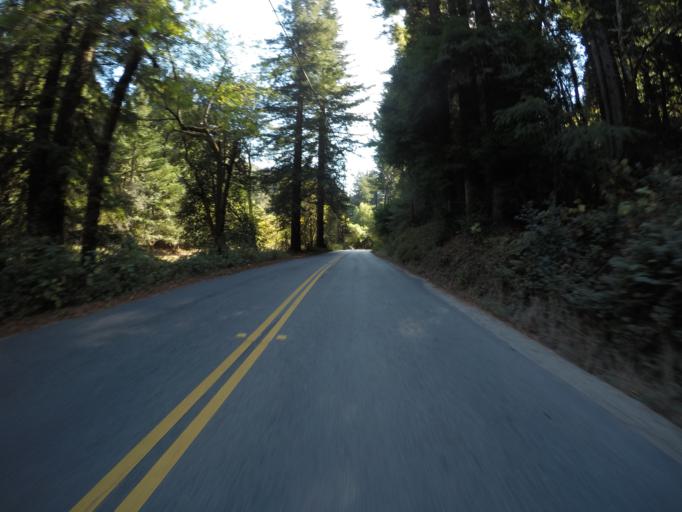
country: US
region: California
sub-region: Santa Cruz County
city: Scotts Valley
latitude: 37.0405
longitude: -121.9976
